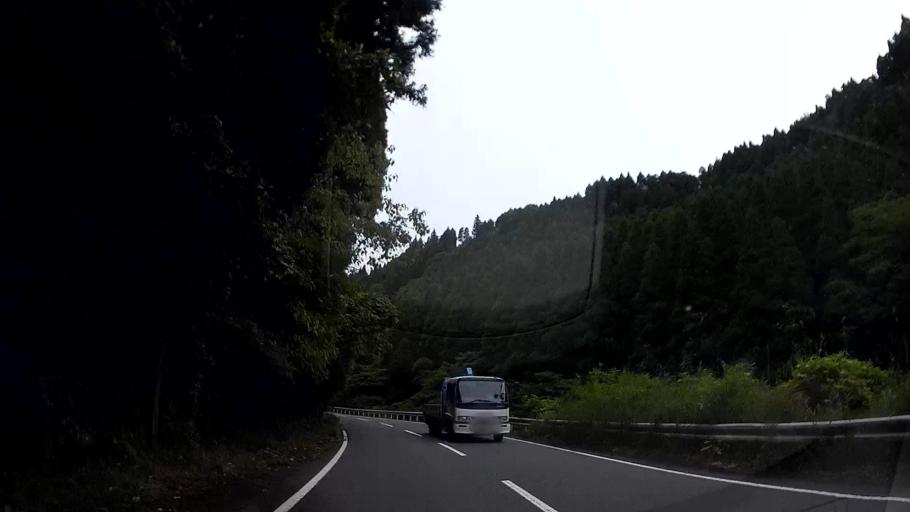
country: JP
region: Kumamoto
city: Kikuchi
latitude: 33.0287
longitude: 130.8928
